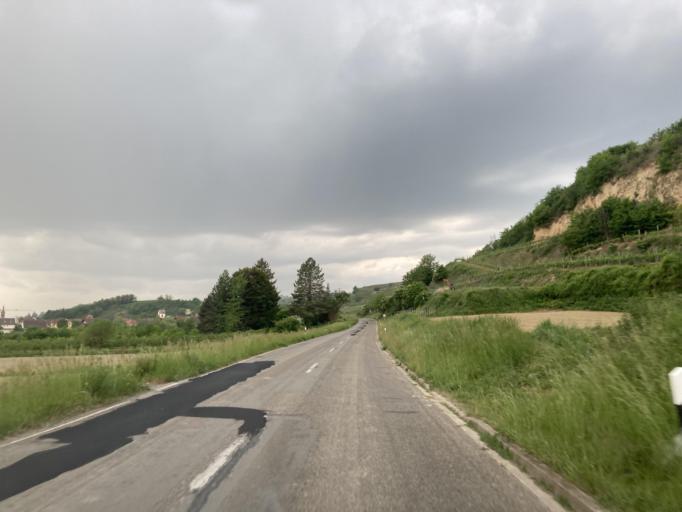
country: DE
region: Baden-Wuerttemberg
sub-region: Freiburg Region
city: Botzingen
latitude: 48.0800
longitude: 7.7332
